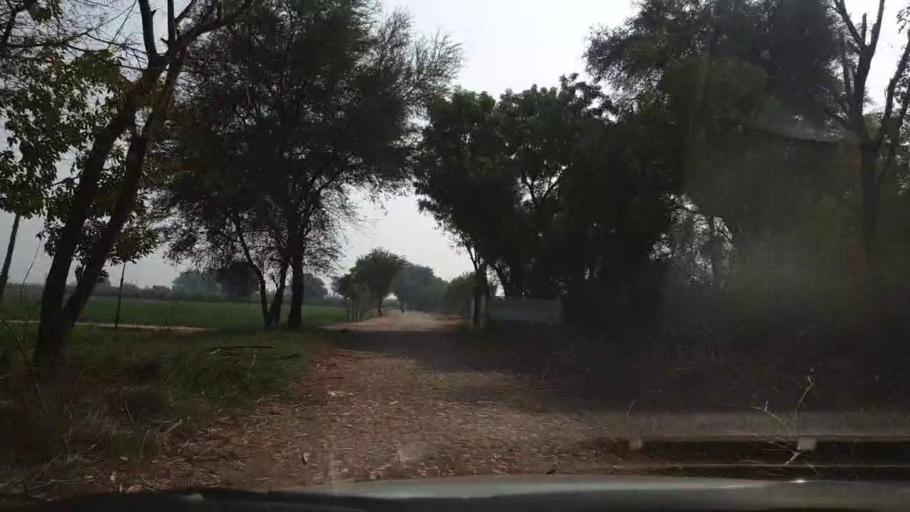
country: PK
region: Sindh
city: Matiari
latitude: 25.6573
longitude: 68.5494
